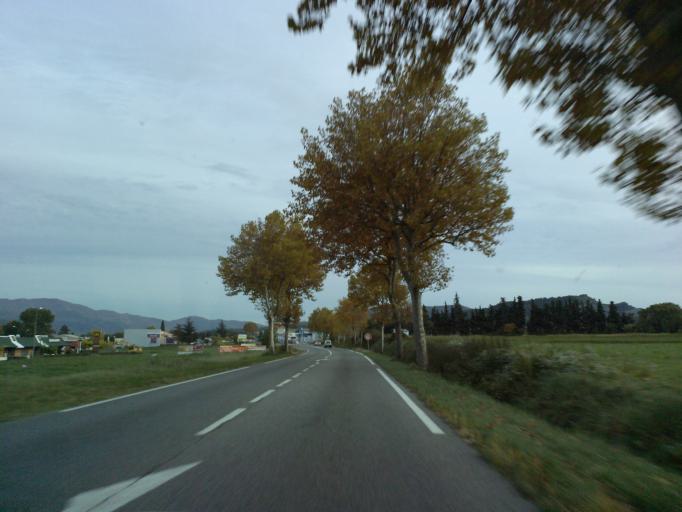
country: FR
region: Provence-Alpes-Cote d'Azur
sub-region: Departement des Alpes-de-Haute-Provence
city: Peipin
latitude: 44.1432
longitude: 5.9644
